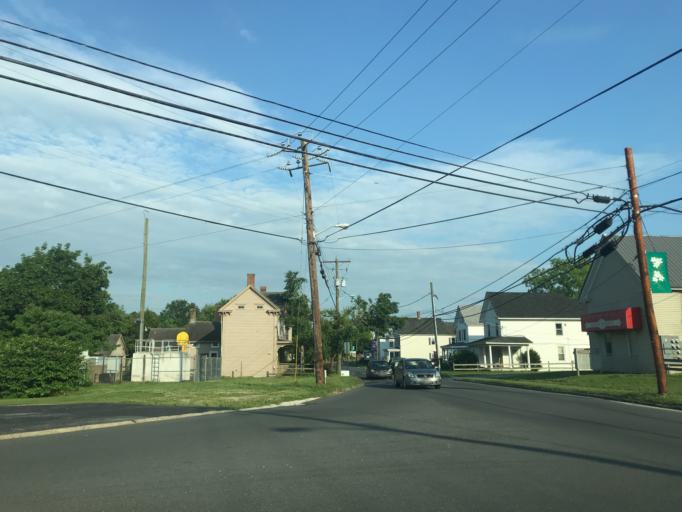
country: US
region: Maryland
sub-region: Caroline County
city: Federalsburg
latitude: 38.6981
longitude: -75.7768
